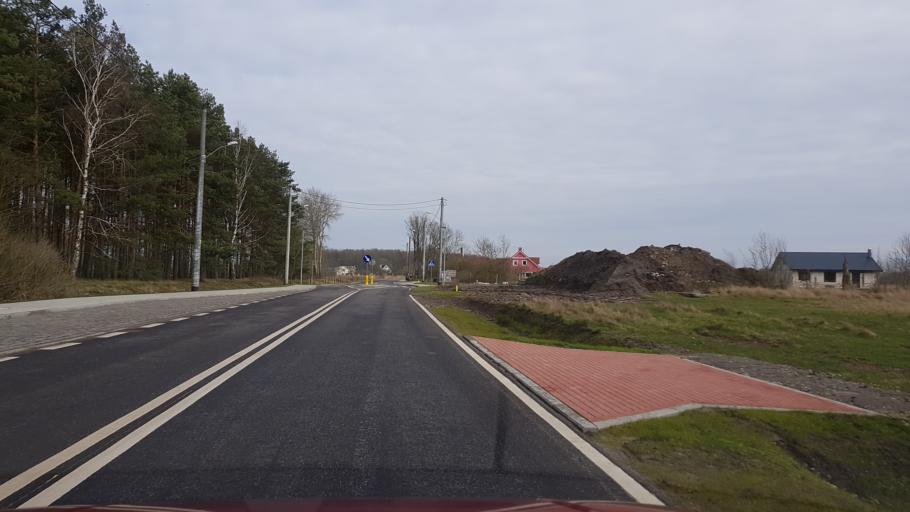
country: PL
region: West Pomeranian Voivodeship
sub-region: Powiat policki
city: Nowe Warpno
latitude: 53.6904
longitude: 14.3555
